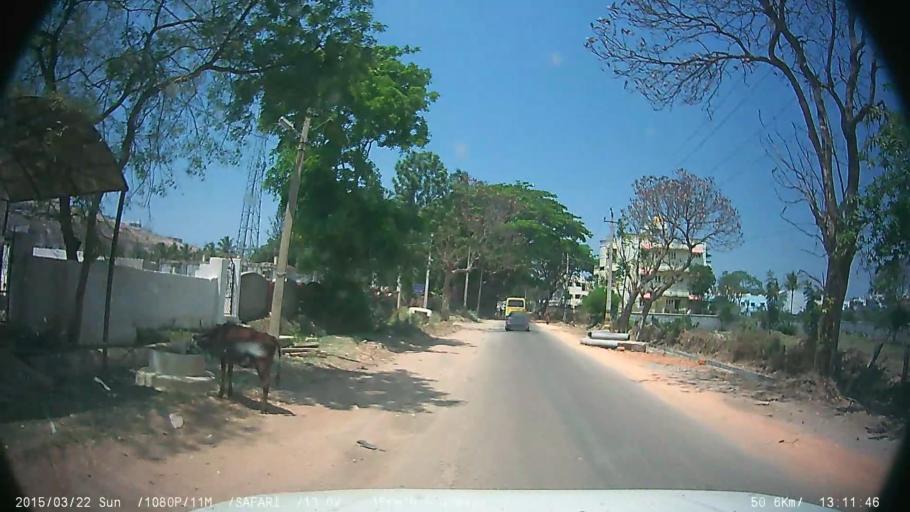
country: IN
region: Karnataka
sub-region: Bangalore Urban
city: Anekal
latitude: 12.8085
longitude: 77.5783
